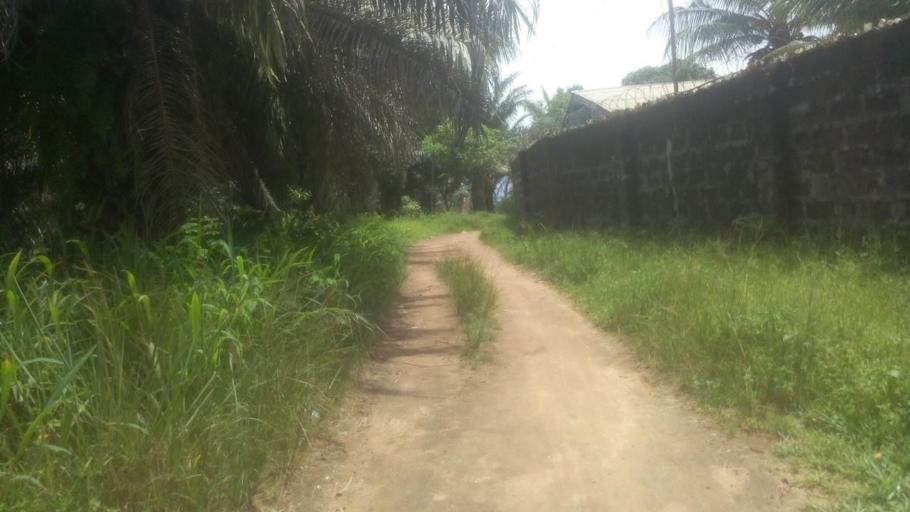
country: SL
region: Northern Province
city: Masoyila
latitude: 8.5468
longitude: -13.1603
